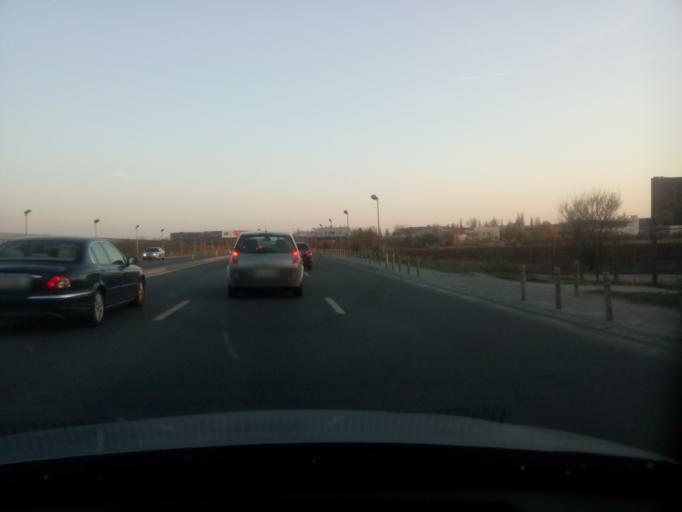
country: RO
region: Ilfov
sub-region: Comuna Otopeni
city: Otopeni
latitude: 44.5653
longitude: 26.0696
